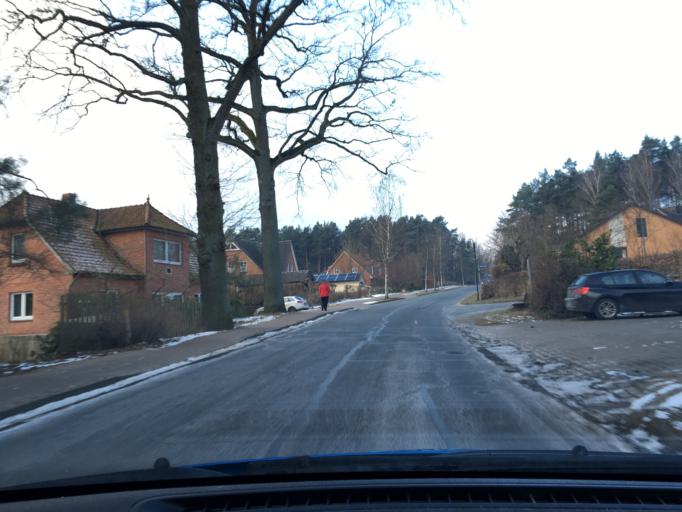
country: DE
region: Lower Saxony
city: Bienenbuttel
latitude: 53.1509
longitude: 10.4860
